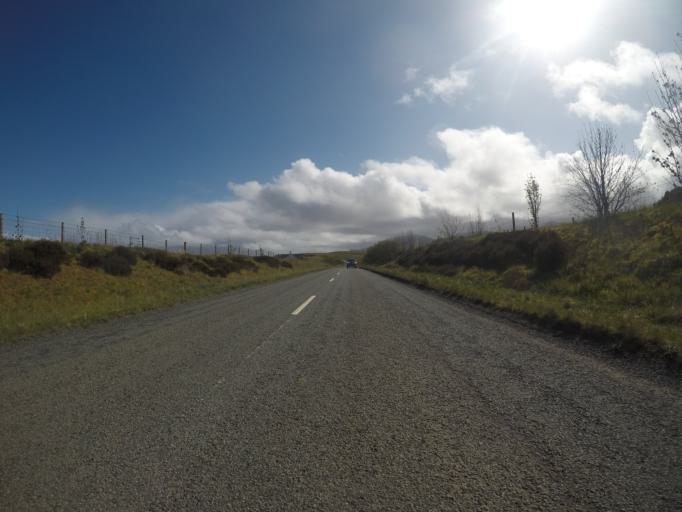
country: GB
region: Scotland
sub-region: Highland
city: Portree
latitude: 57.5828
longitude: -6.1578
